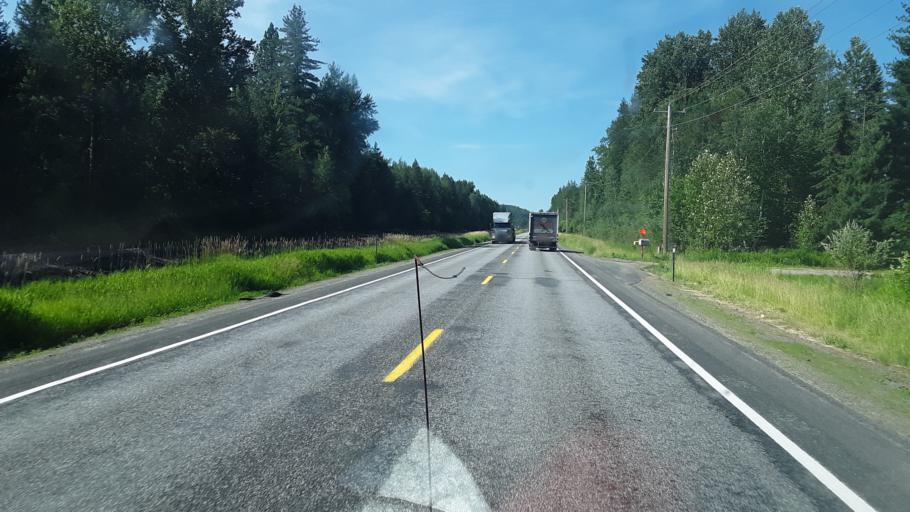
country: US
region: Idaho
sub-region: Bonner County
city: Ponderay
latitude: 48.4428
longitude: -116.4848
